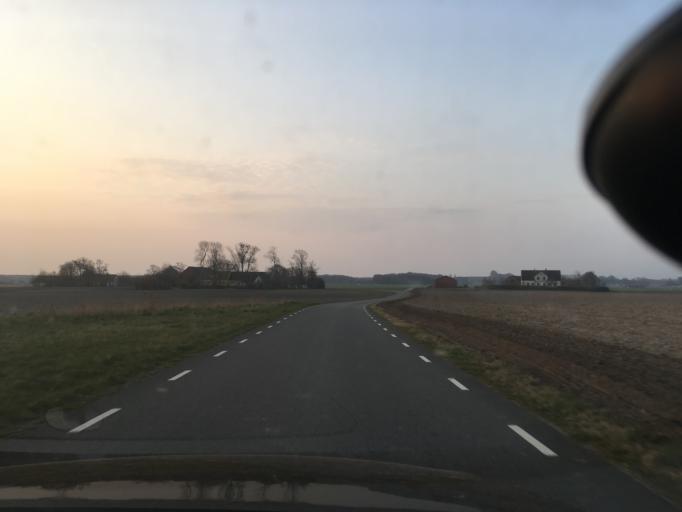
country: SE
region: Skane
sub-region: Ystads Kommun
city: Kopingebro
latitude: 55.4120
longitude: 14.1524
